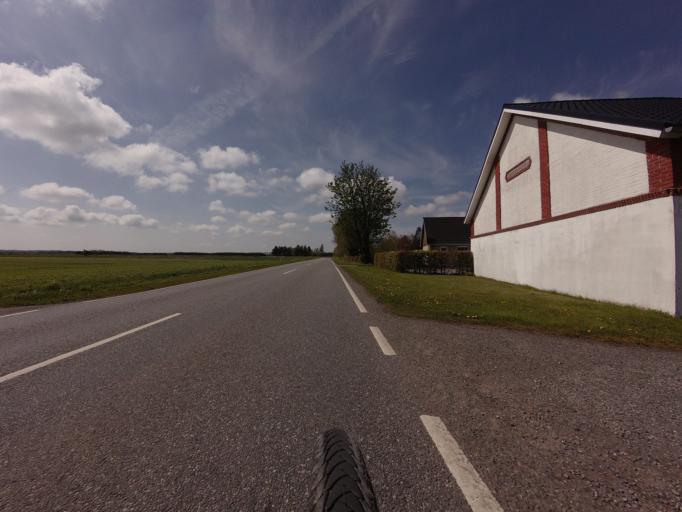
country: DK
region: North Denmark
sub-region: Jammerbugt Kommune
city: Brovst
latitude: 57.1444
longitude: 9.5368
